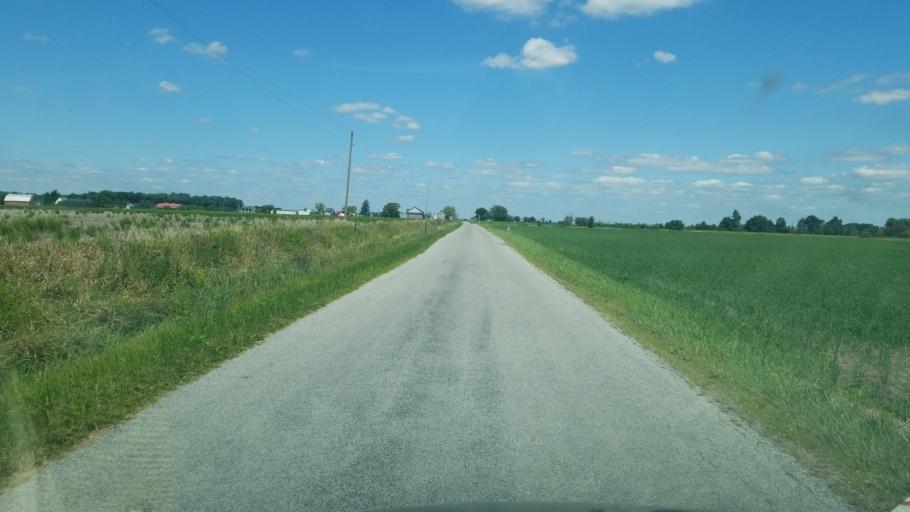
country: US
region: Ohio
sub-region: Fulton County
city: Delta
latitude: 41.6574
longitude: -84.0160
